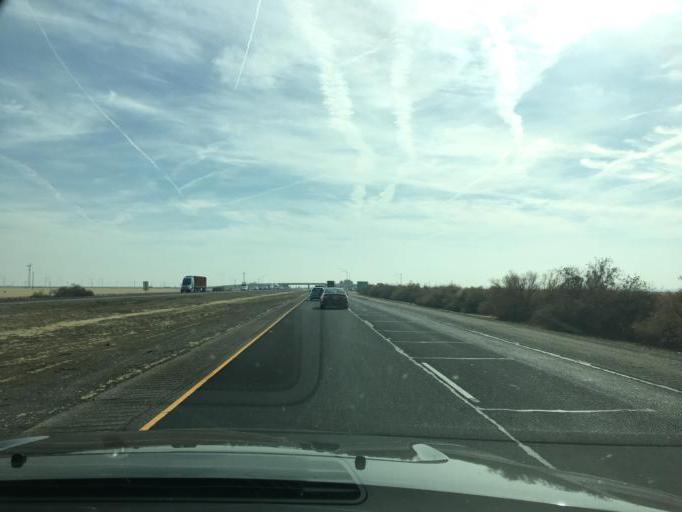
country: US
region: California
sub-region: Kern County
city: Lost Hills
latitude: 35.7381
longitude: -119.7441
